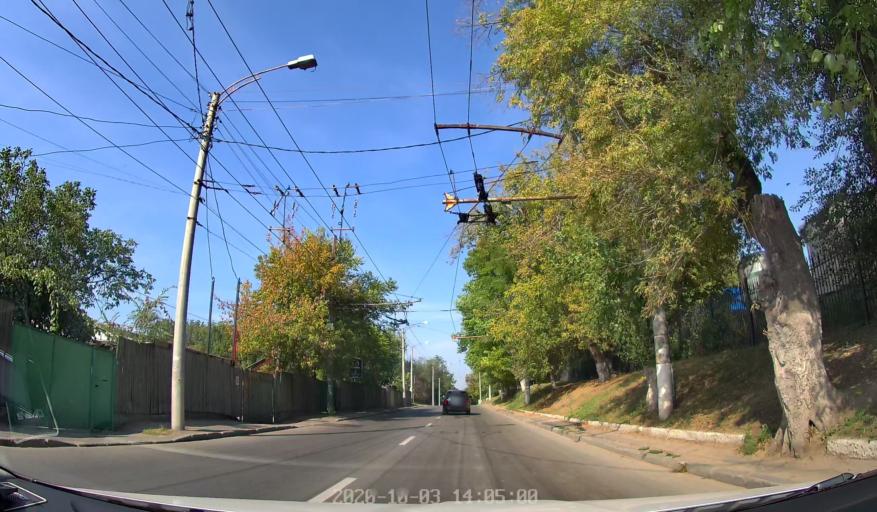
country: MD
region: Chisinau
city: Chisinau
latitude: 47.0295
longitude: 28.8171
